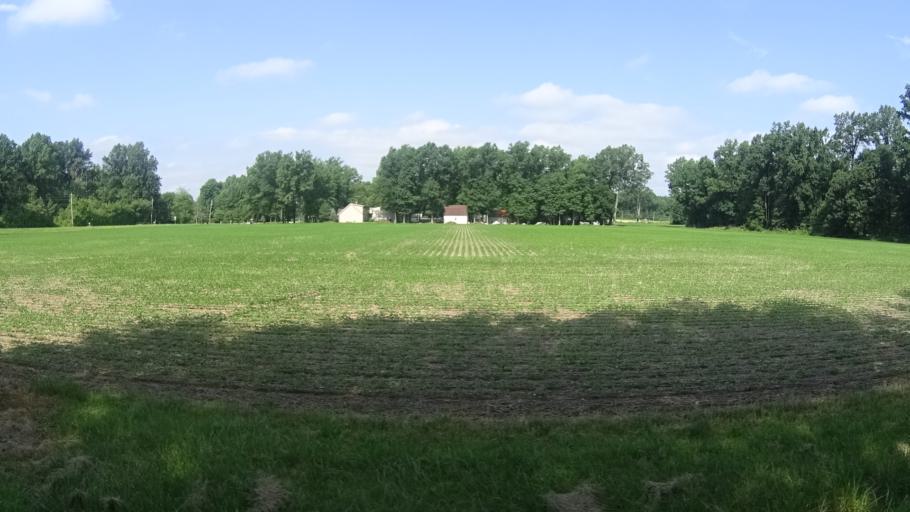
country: US
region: Ohio
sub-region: Lorain County
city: Vermilion
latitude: 41.3655
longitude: -82.4303
